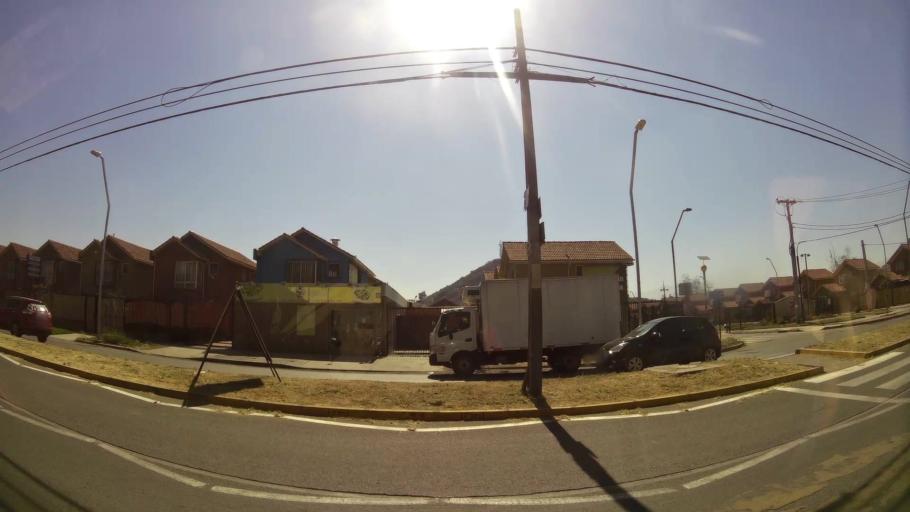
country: CL
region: Santiago Metropolitan
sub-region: Provincia de Maipo
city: San Bernardo
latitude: -33.6143
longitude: -70.6828
